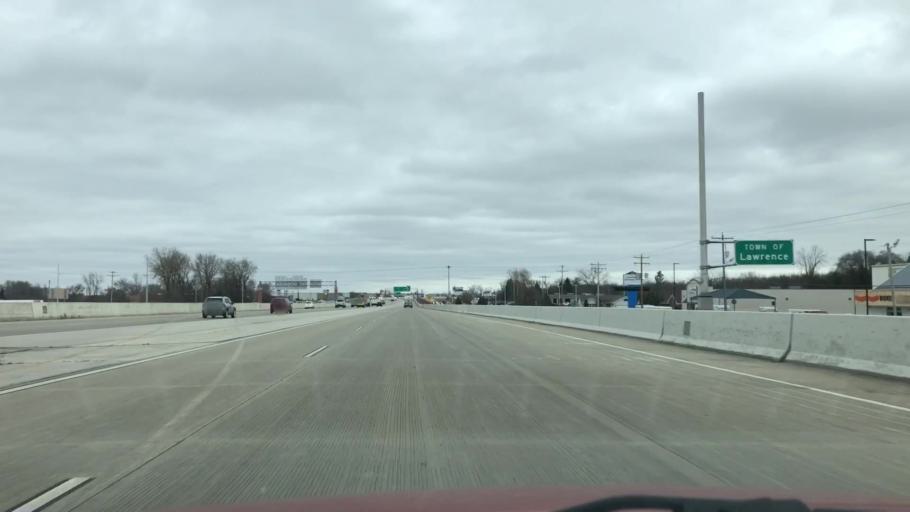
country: US
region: Wisconsin
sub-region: Brown County
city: De Pere
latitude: 44.4509
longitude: -88.0915
